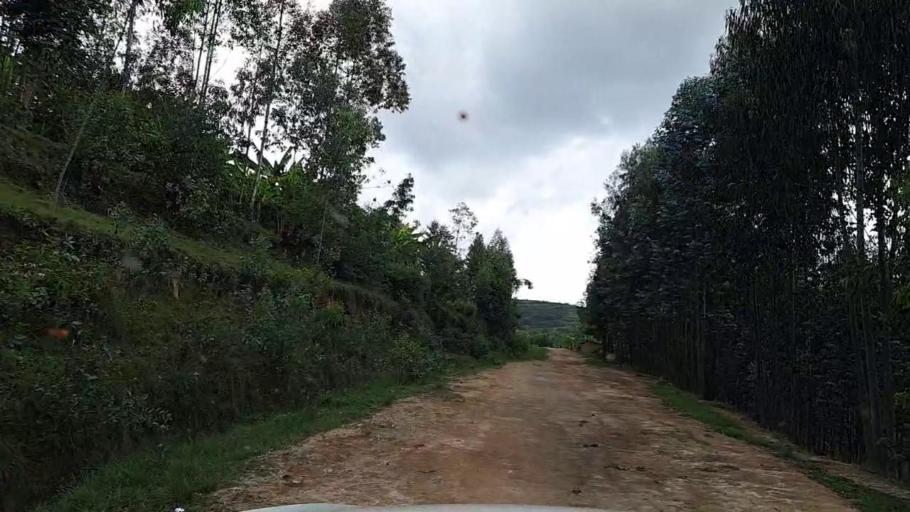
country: RW
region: Southern Province
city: Gikongoro
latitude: -2.3932
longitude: 29.5522
